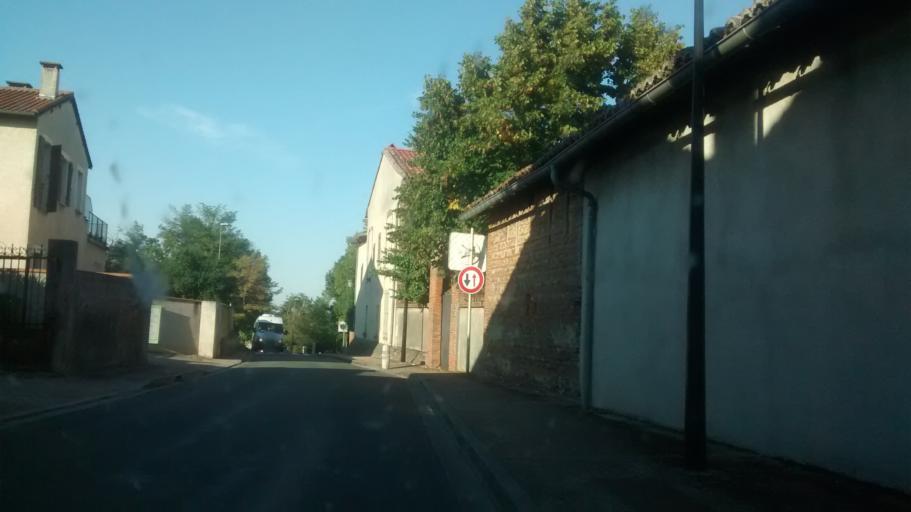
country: FR
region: Midi-Pyrenees
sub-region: Departement de la Haute-Garonne
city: Lherm
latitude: 43.4304
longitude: 1.2243
